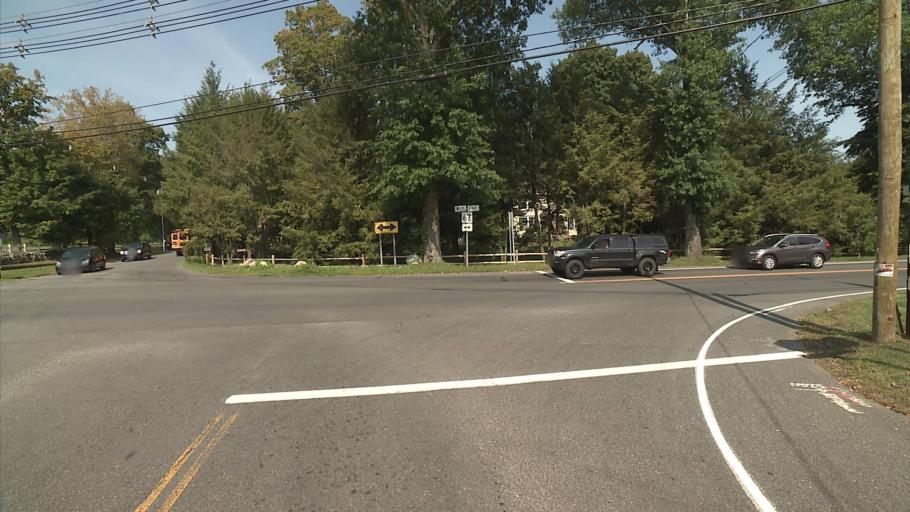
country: US
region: Connecticut
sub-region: New Haven County
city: Heritage Village
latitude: 41.5097
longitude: -73.2468
